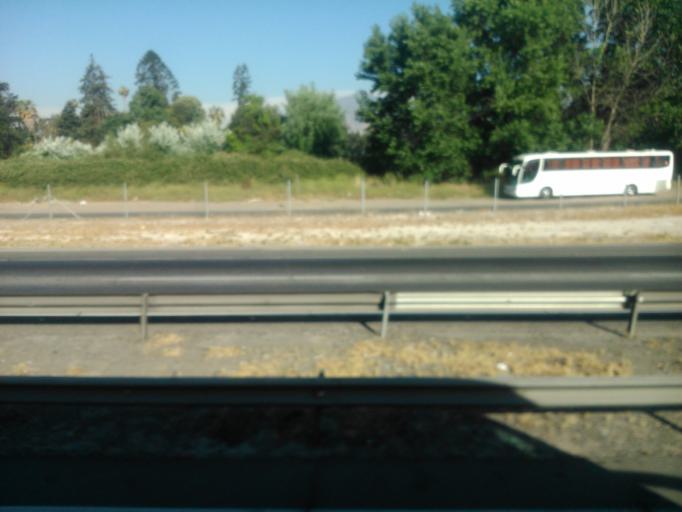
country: CL
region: Santiago Metropolitan
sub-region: Provincia de Maipo
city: Buin
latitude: -33.7162
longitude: -70.7260
